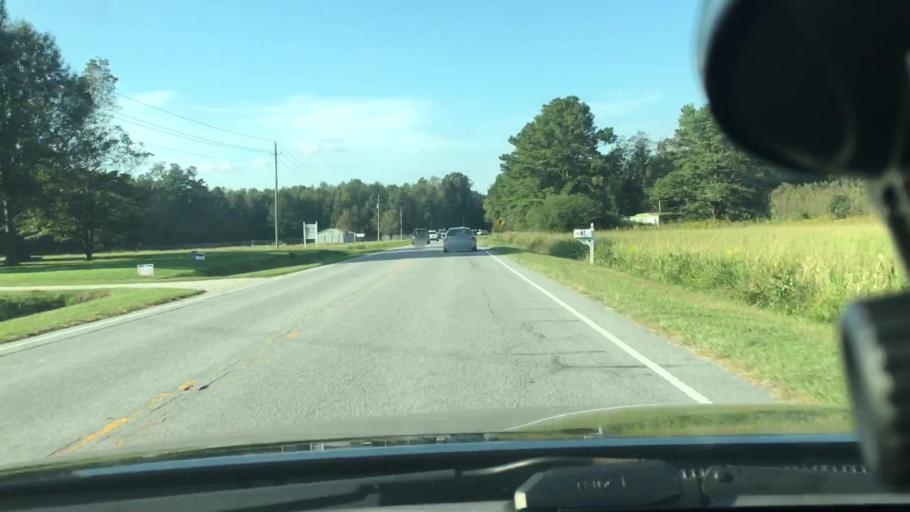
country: US
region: North Carolina
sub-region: Pitt County
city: Windsor
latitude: 35.4322
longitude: -77.2624
